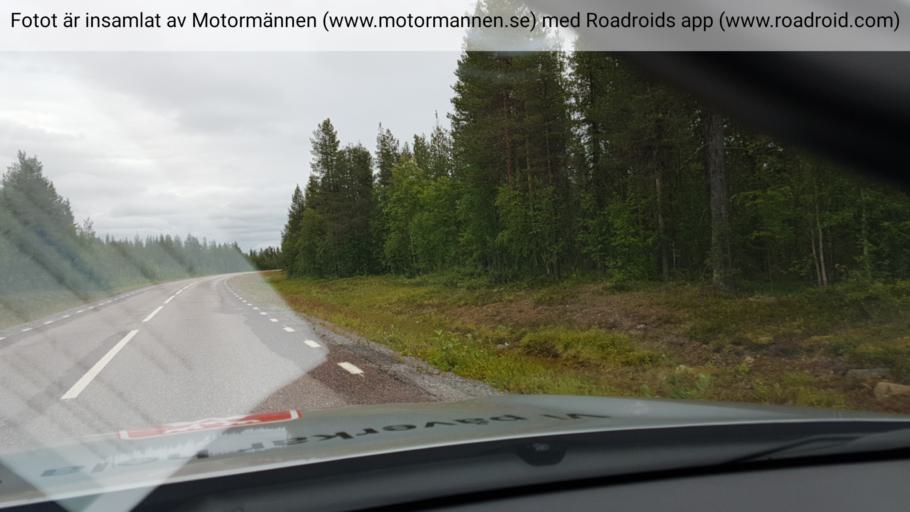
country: SE
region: Norrbotten
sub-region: Gallivare Kommun
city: Gaellivare
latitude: 67.0744
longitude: 21.4552
